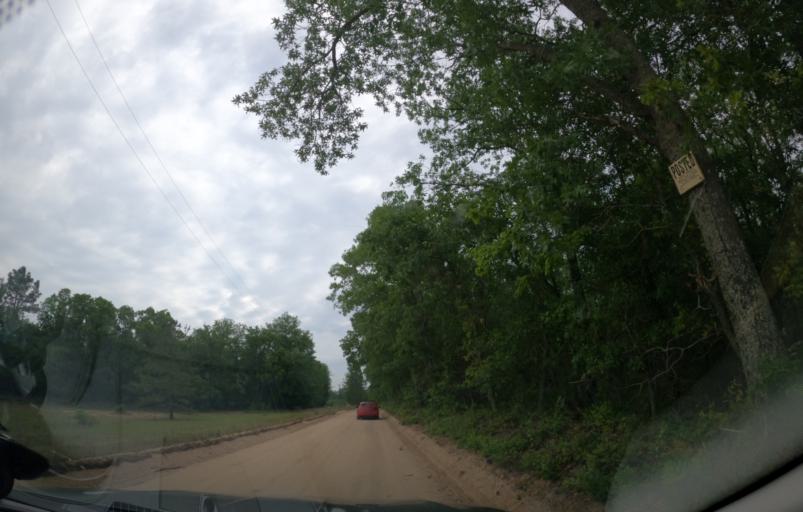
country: US
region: South Carolina
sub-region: Lexington County
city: Gaston
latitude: 33.6472
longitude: -81.2575
